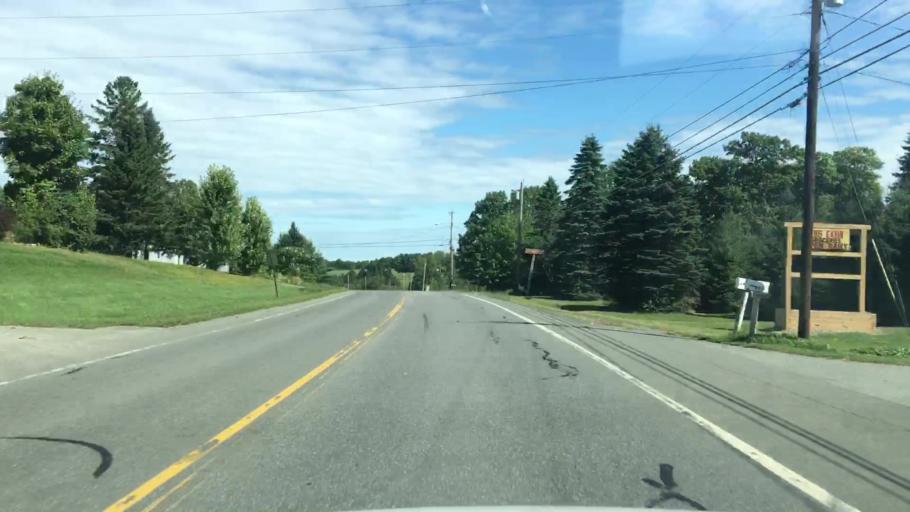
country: US
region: Maine
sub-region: Penobscot County
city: Dexter
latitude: 45.0693
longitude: -69.2388
